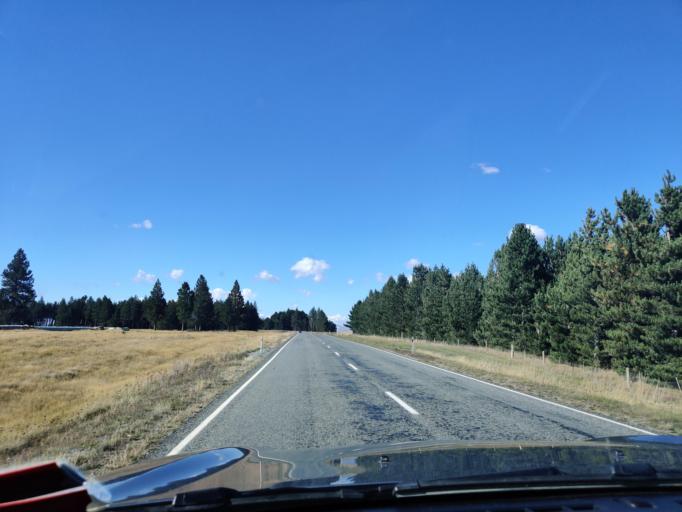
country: NZ
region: Canterbury
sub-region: Timaru District
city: Pleasant Point
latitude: -44.1823
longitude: 170.3137
